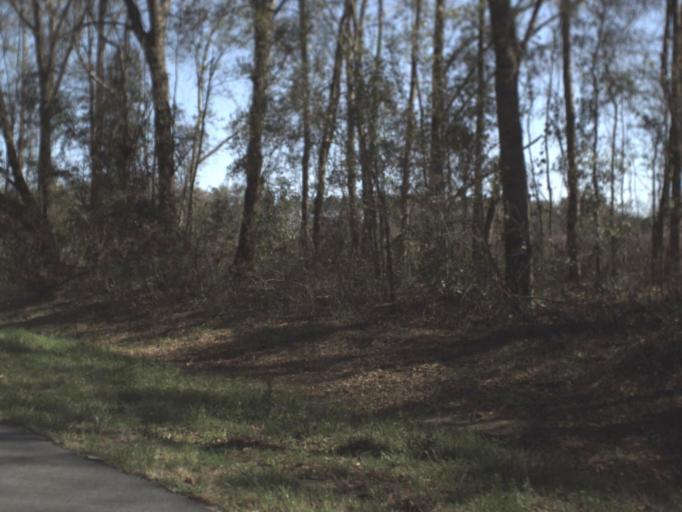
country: US
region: Florida
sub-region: Jefferson County
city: Monticello
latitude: 30.4320
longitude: -84.0196
